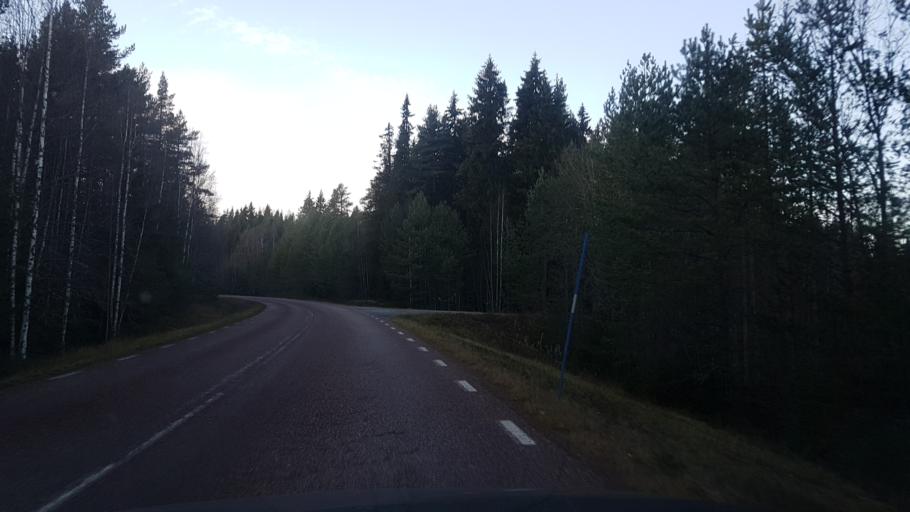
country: SE
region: Dalarna
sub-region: Rattviks Kommun
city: Raettvik
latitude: 60.7433
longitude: 15.2252
